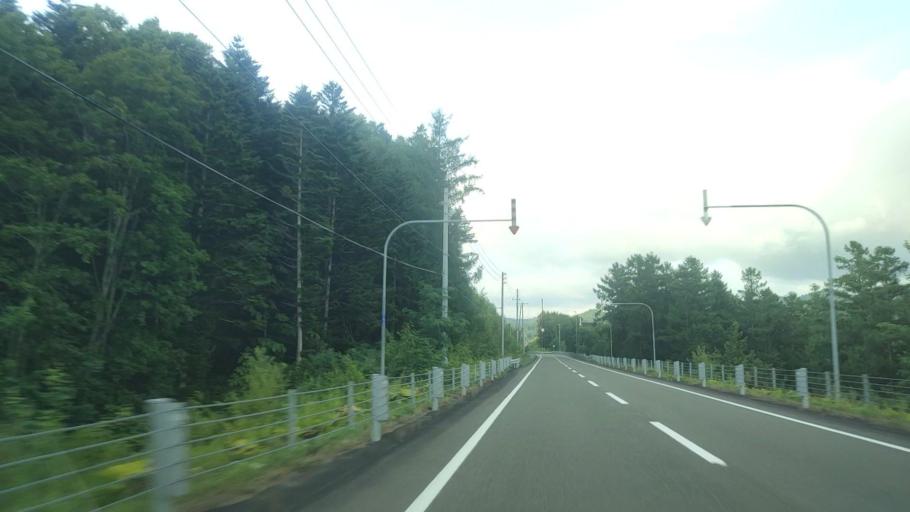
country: JP
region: Hokkaido
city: Bibai
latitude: 43.0663
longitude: 142.1020
